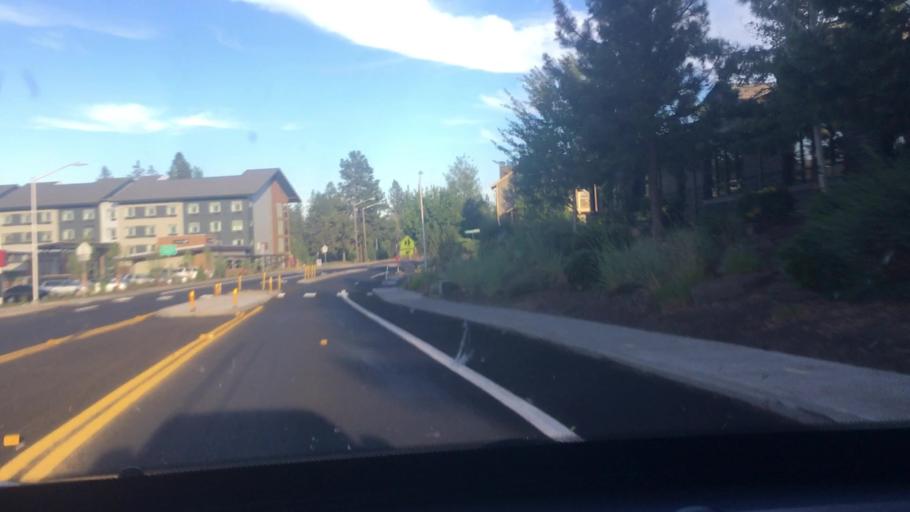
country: US
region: Oregon
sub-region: Deschutes County
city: Bend
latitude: 44.0396
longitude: -121.3381
